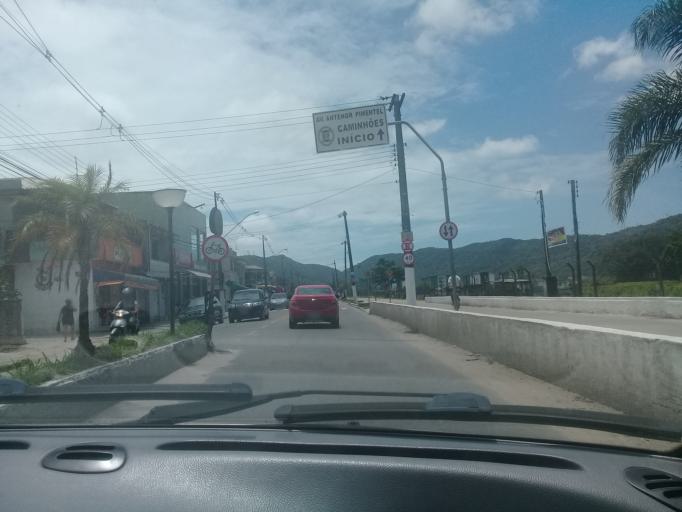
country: BR
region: Sao Paulo
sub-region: Guaruja
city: Guaruja
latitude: -23.9679
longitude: -46.2587
